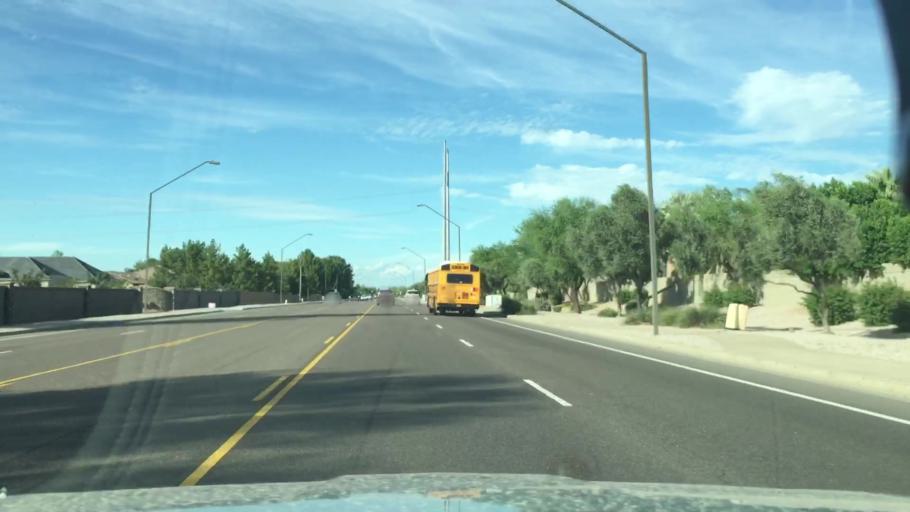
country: US
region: Arizona
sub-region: Maricopa County
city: Gilbert
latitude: 33.3549
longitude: -111.7385
